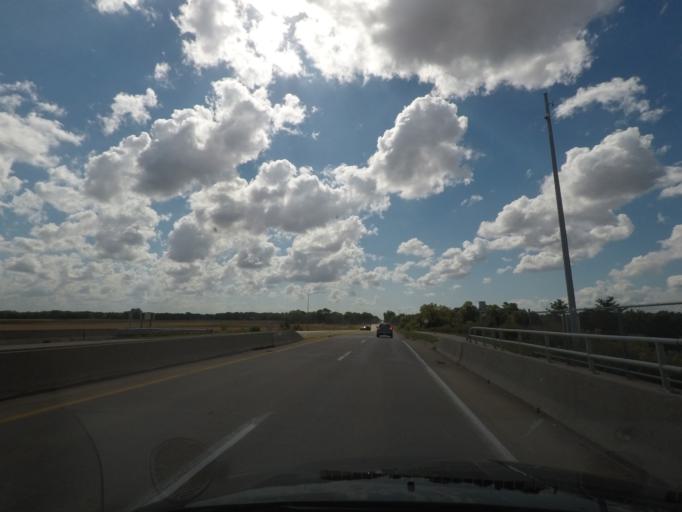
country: US
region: Iowa
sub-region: Story County
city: Ames
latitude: 42.0082
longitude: -93.6788
